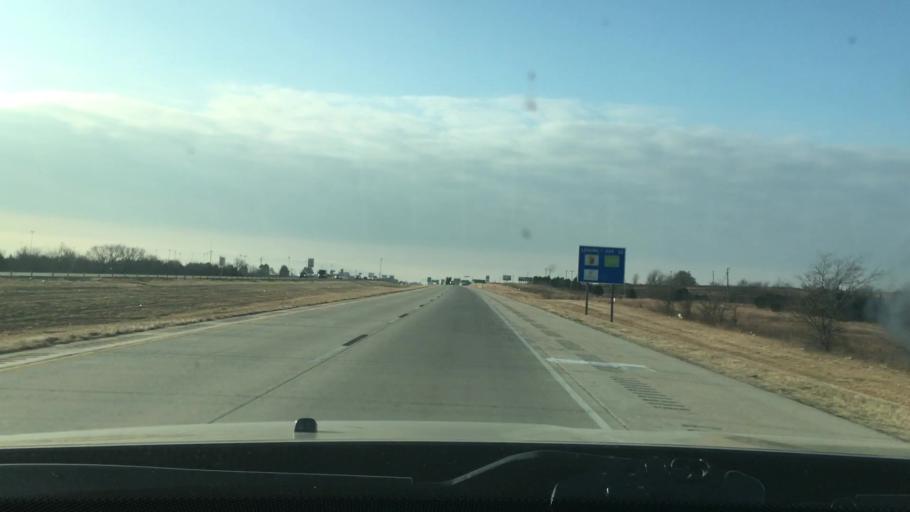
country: US
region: Oklahoma
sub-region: Carter County
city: Ardmore
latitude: 34.2161
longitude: -97.1642
